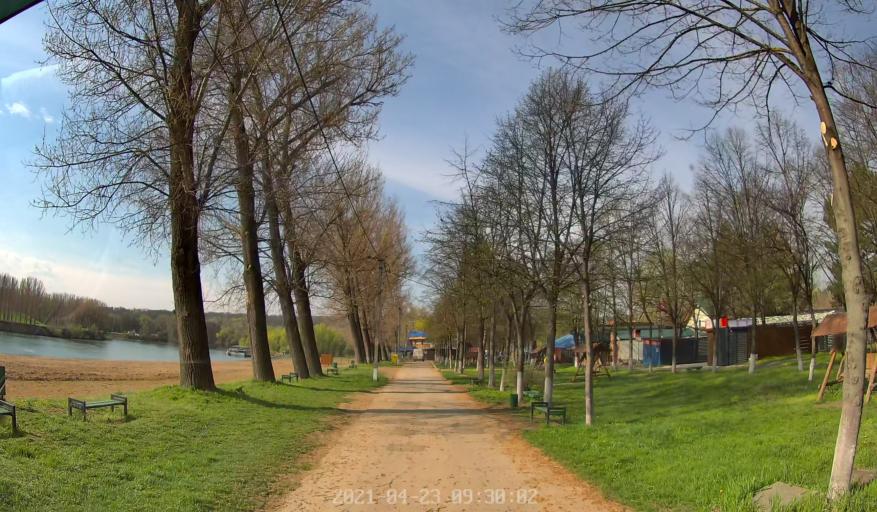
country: MD
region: Chisinau
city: Vadul lui Voda
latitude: 47.0843
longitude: 29.1119
